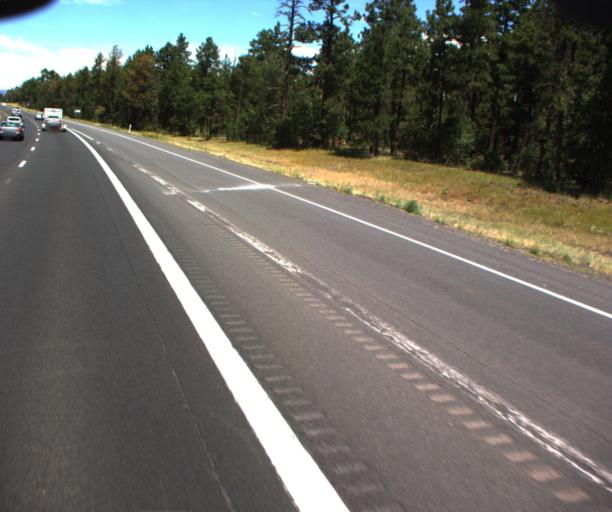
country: US
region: Arizona
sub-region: Coconino County
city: Sedona
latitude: 34.8570
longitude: -111.6097
